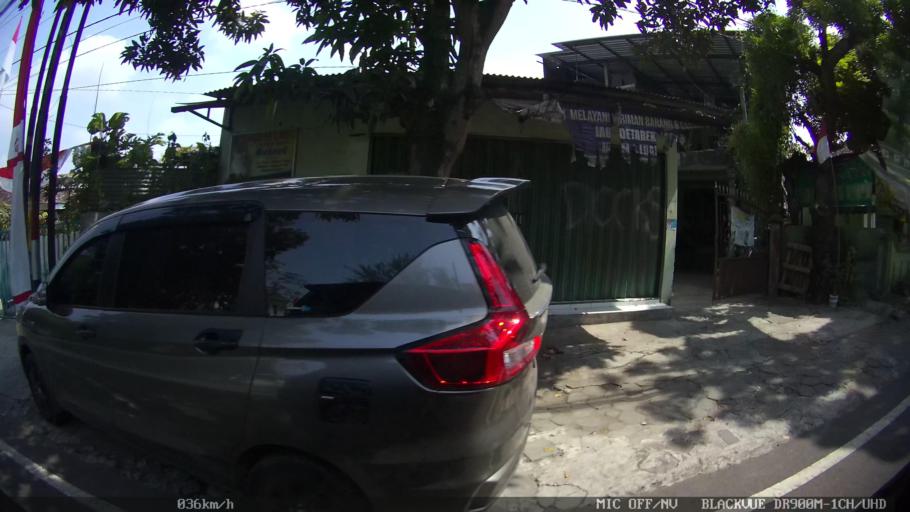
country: ID
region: Daerah Istimewa Yogyakarta
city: Yogyakarta
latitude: -7.8083
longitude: 110.3936
